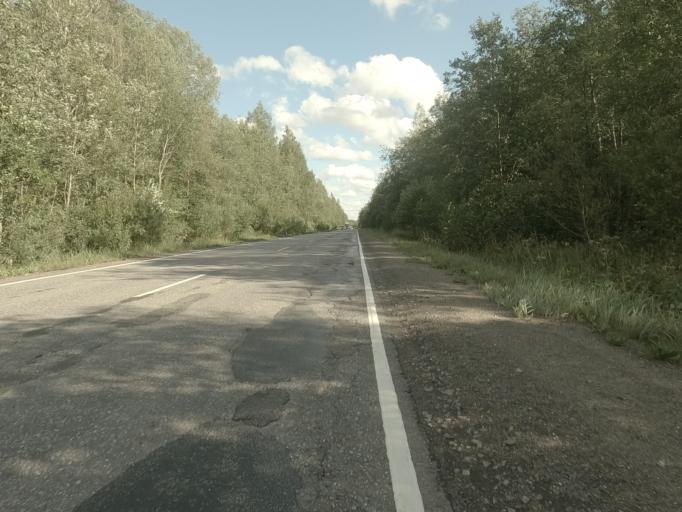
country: RU
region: Leningrad
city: Shcheglovo
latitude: 59.9950
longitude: 30.8780
